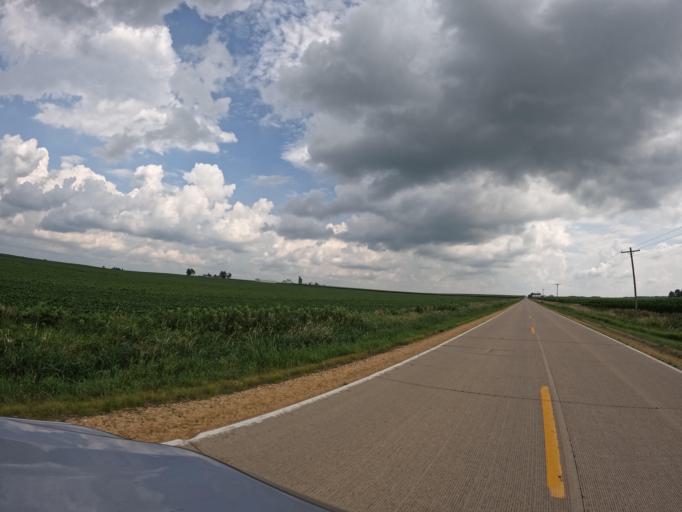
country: US
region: Iowa
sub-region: Clinton County
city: De Witt
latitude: 41.7839
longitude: -90.4131
